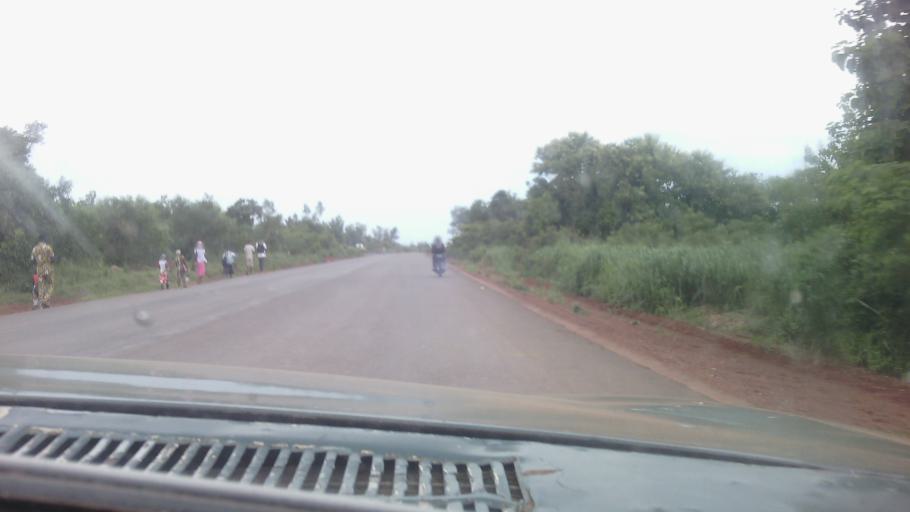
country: BJ
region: Mono
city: Come
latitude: 6.5294
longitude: 1.8184
